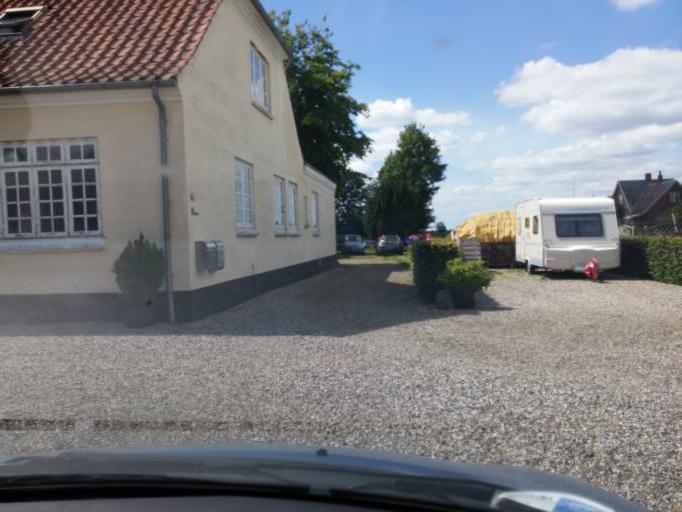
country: DK
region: South Denmark
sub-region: Kerteminde Kommune
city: Munkebo
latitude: 55.4186
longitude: 10.5728
